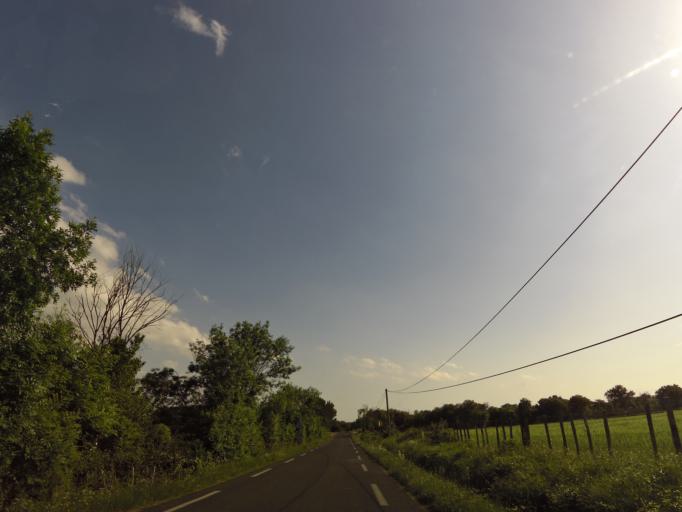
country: FR
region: Languedoc-Roussillon
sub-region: Departement du Gard
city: Aubais
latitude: 43.7571
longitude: 4.1133
